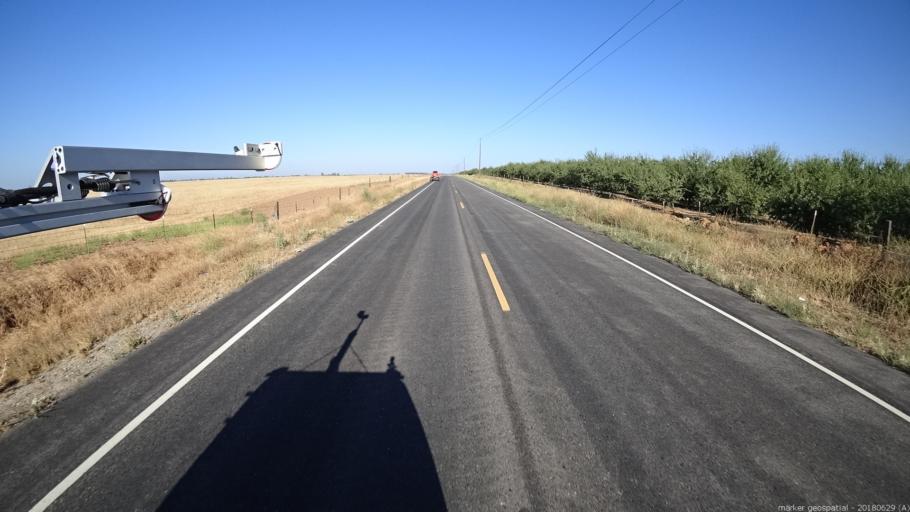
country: US
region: California
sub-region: Madera County
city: Parksdale
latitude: 36.9667
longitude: -119.9811
